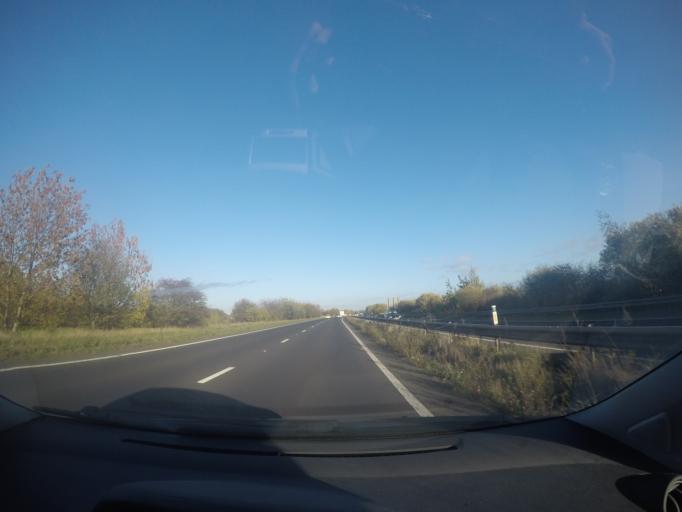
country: GB
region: England
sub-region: City of York
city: Copmanthorpe
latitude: 53.9228
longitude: -1.1294
